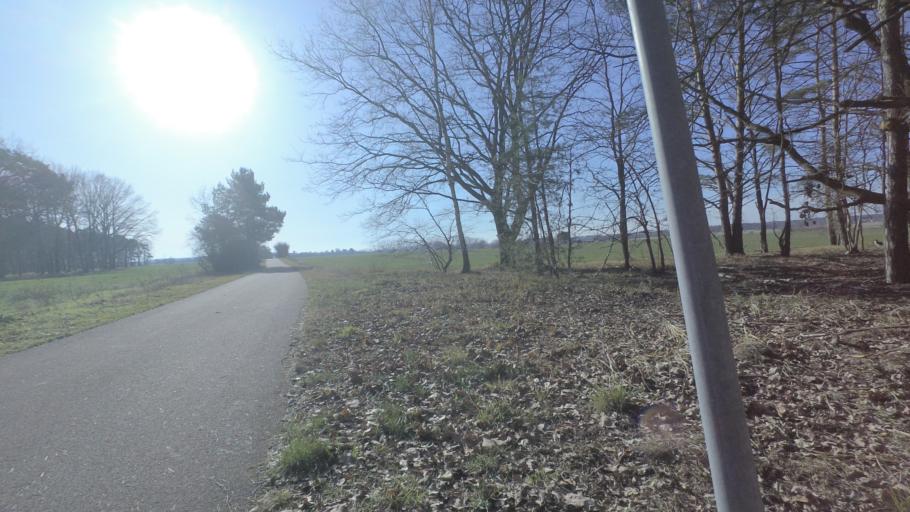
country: DE
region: Brandenburg
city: Juterbog
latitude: 52.0215
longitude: 13.1281
